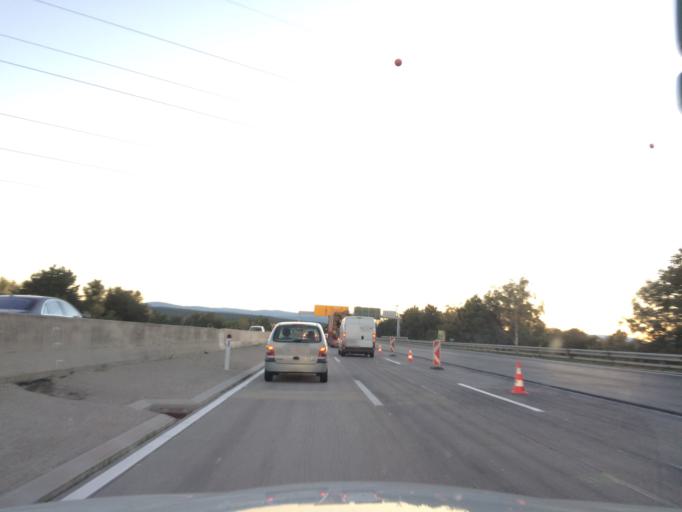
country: AT
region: Lower Austria
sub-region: Politischer Bezirk Neunkirchen
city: Breitenau
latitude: 47.7216
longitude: 16.1412
